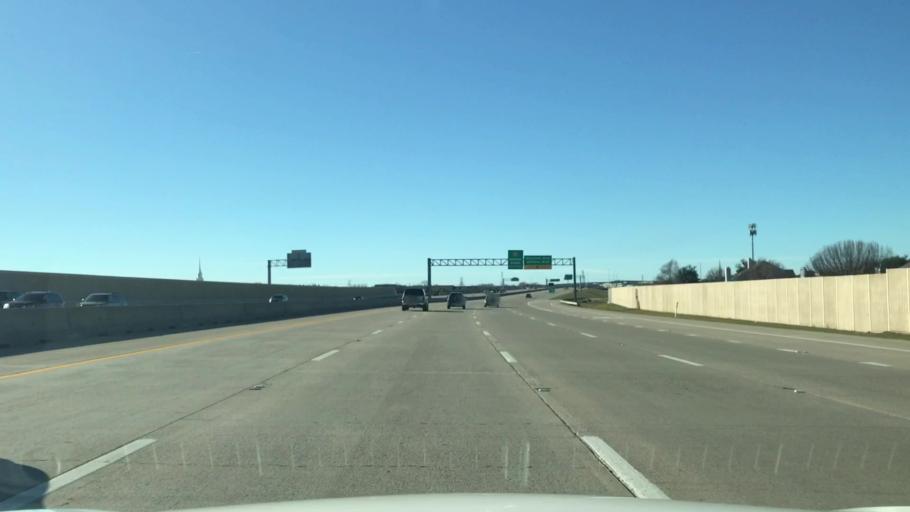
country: US
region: Texas
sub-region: Denton County
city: Lewisville
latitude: 33.0164
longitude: -96.9388
